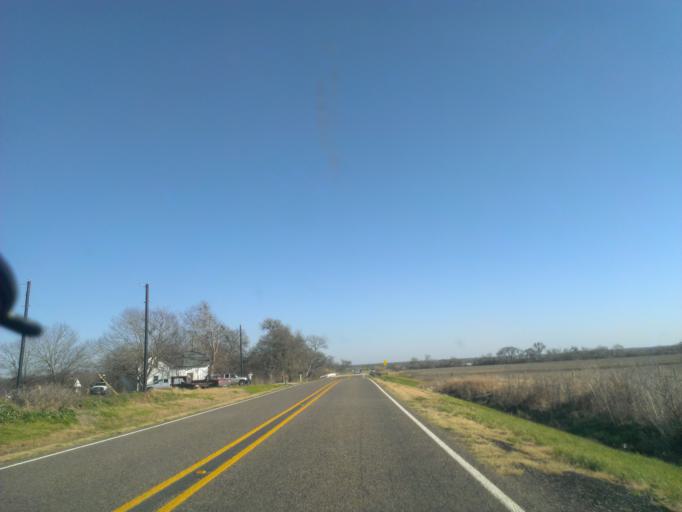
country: US
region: Texas
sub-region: Milam County
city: Thorndale
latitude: 30.5394
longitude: -97.2638
